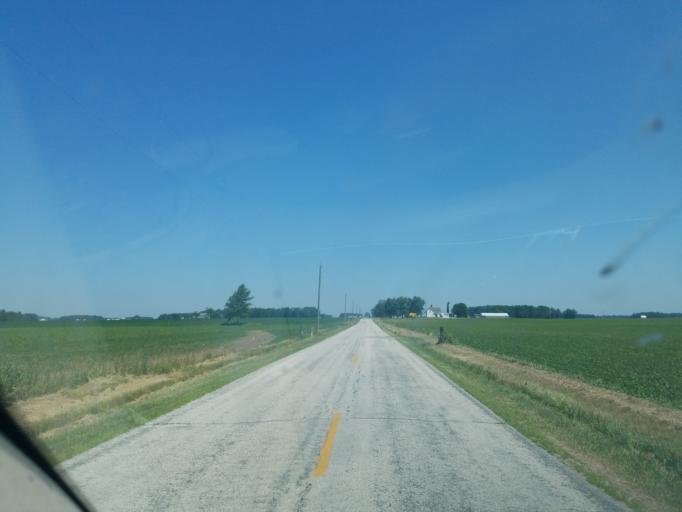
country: US
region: Ohio
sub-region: Mercer County
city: Coldwater
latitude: 40.5766
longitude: -84.7084
